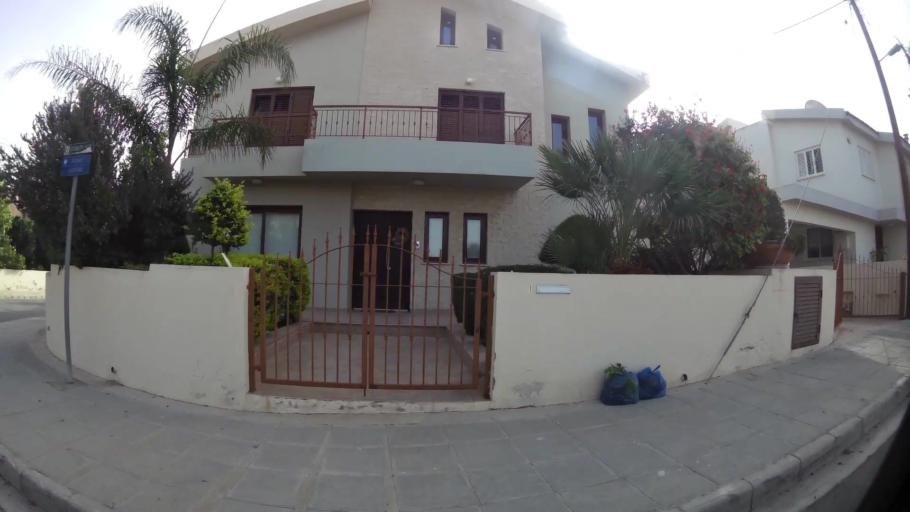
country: CY
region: Lefkosia
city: Geri
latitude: 35.0745
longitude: 33.3863
